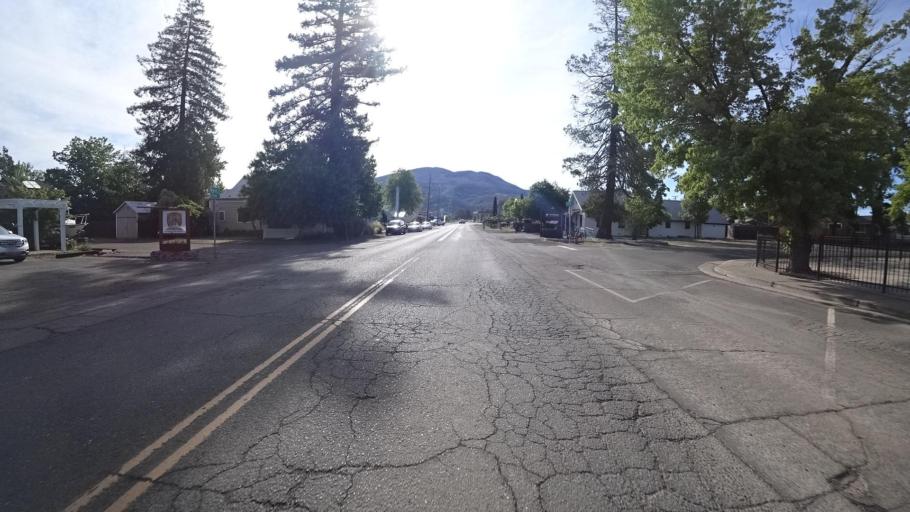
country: US
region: California
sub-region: Lake County
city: Kelseyville
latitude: 38.9776
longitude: -122.8364
